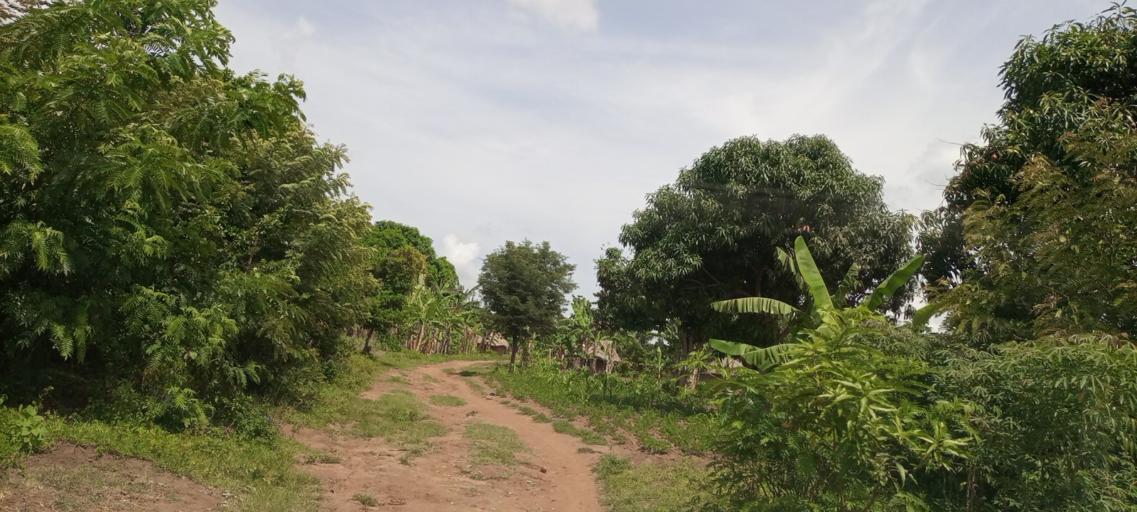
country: UG
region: Eastern Region
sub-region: Budaka District
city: Budaka
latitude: 1.1718
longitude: 33.9488
